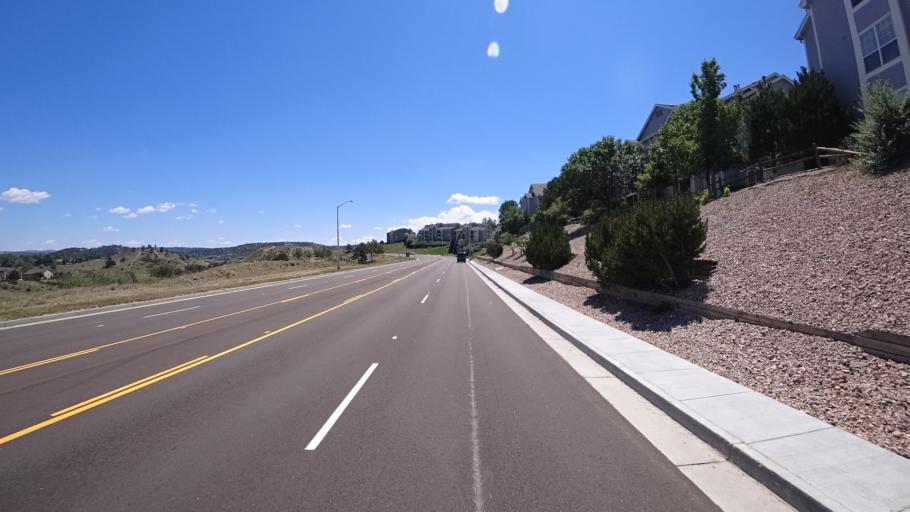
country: US
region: Colorado
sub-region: El Paso County
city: Air Force Academy
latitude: 38.9182
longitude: -104.8354
